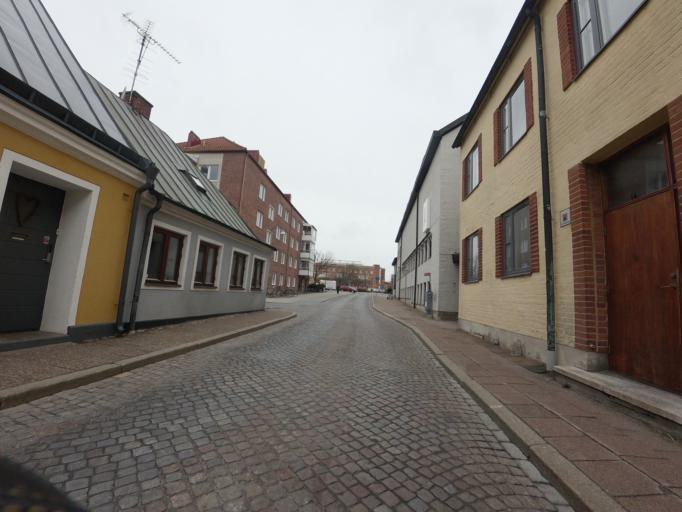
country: SE
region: Skane
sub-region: Ystads Kommun
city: Ystad
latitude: 55.4319
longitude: 13.8186
